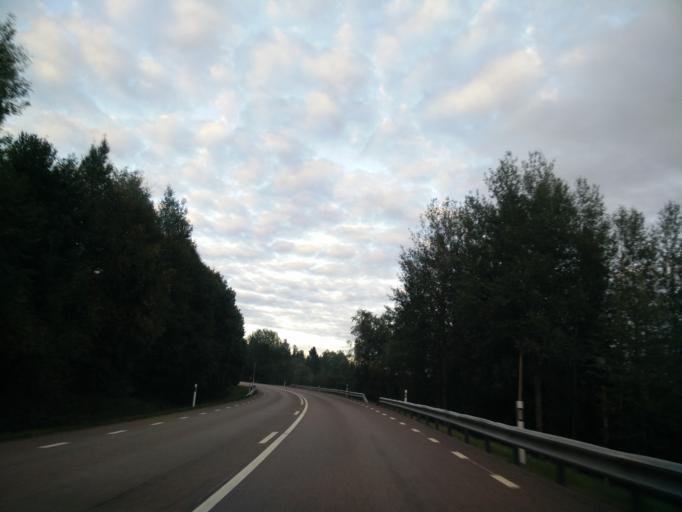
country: SE
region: Vaesternorrland
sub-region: Kramfors Kommun
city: Nordingra
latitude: 62.9197
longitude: 18.0622
